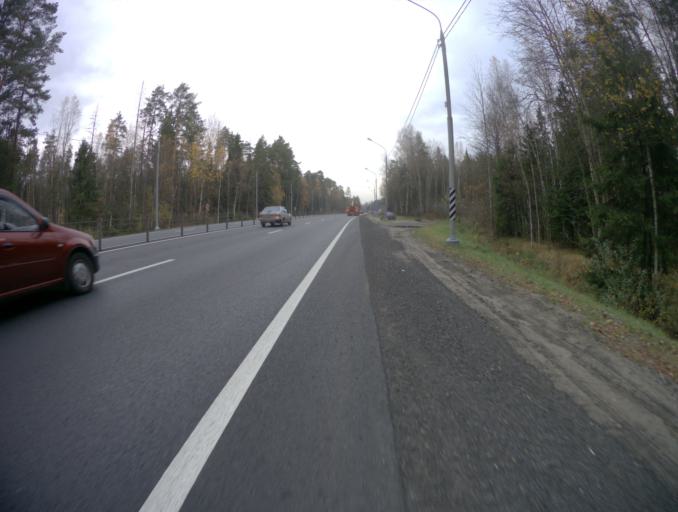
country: RU
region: Moskovskaya
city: Malaya Dubna
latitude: 55.8636
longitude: 38.9628
